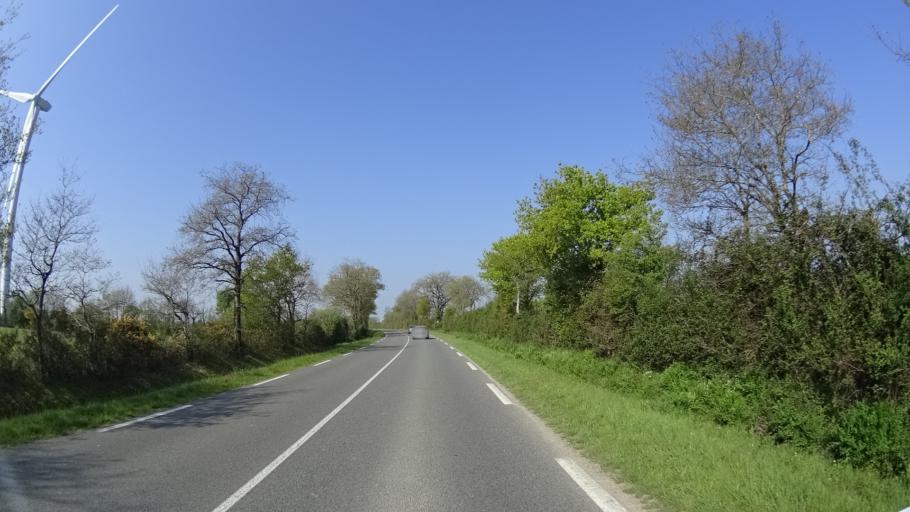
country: FR
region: Pays de la Loire
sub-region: Departement de la Loire-Atlantique
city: Saint-Hilaire-de-Chaleons
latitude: 47.0764
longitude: -1.8806
